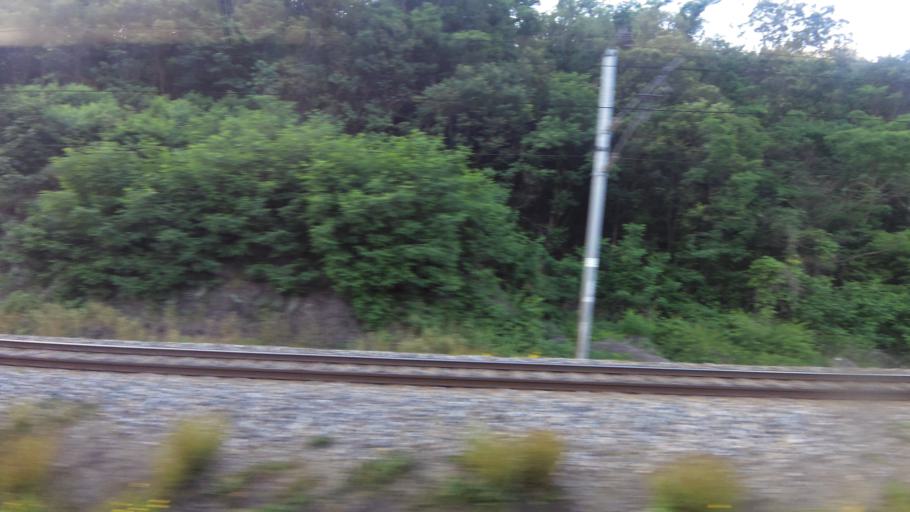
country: KR
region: Chungcheongbuk-do
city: Yong-dong
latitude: 36.1802
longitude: 127.8311
